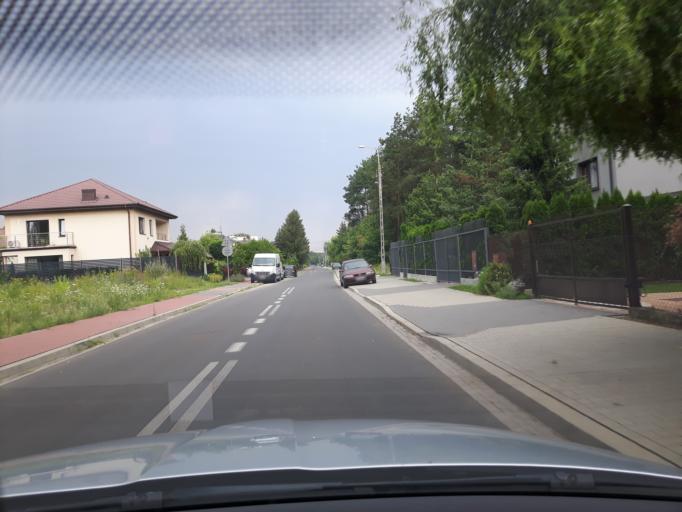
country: PL
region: Masovian Voivodeship
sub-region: Powiat wolominski
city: Zabki
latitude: 52.2940
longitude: 21.1304
